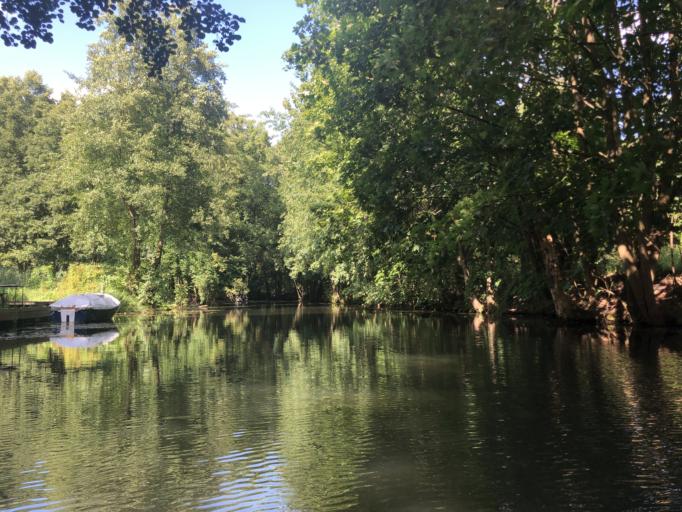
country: DE
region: Brandenburg
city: Mullrose
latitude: 52.2454
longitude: 14.4297
